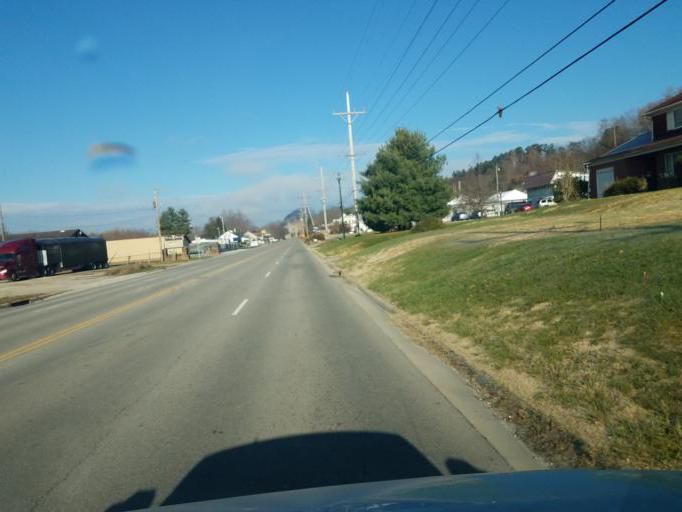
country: US
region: Ohio
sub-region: Scioto County
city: Wheelersburg
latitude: 38.7395
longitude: -82.8638
